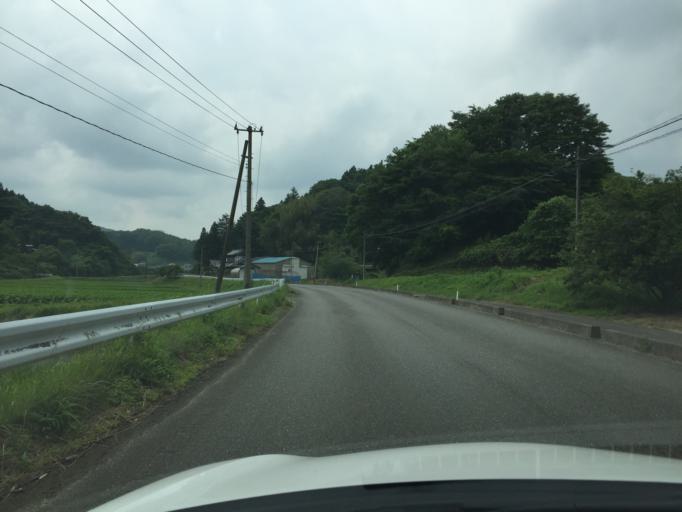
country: JP
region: Fukushima
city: Funehikimachi-funehiki
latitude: 37.2926
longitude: 140.5848
